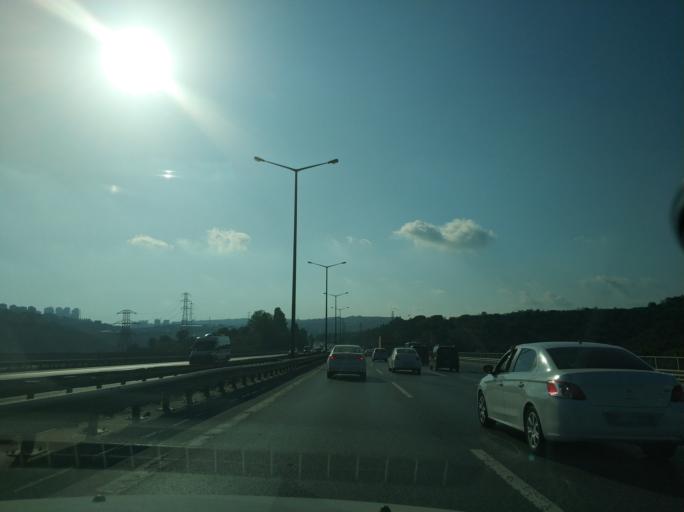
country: TR
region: Istanbul
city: Sisli
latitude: 41.0929
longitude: 28.9348
